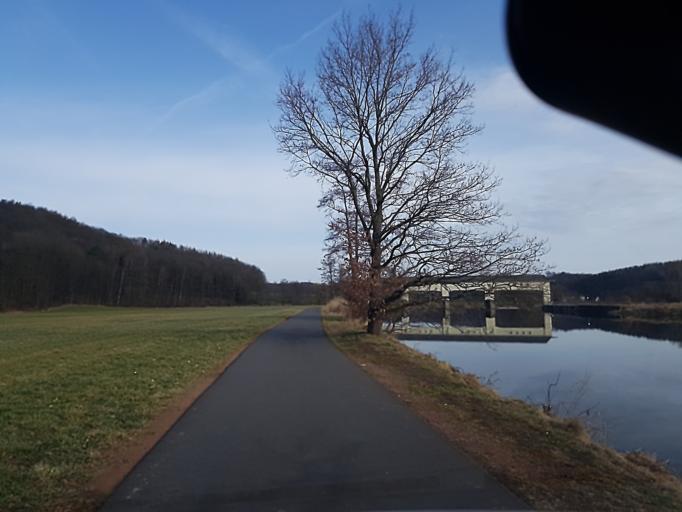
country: DE
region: Saxony
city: Grossweitzschen
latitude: 51.1432
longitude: 13.0083
